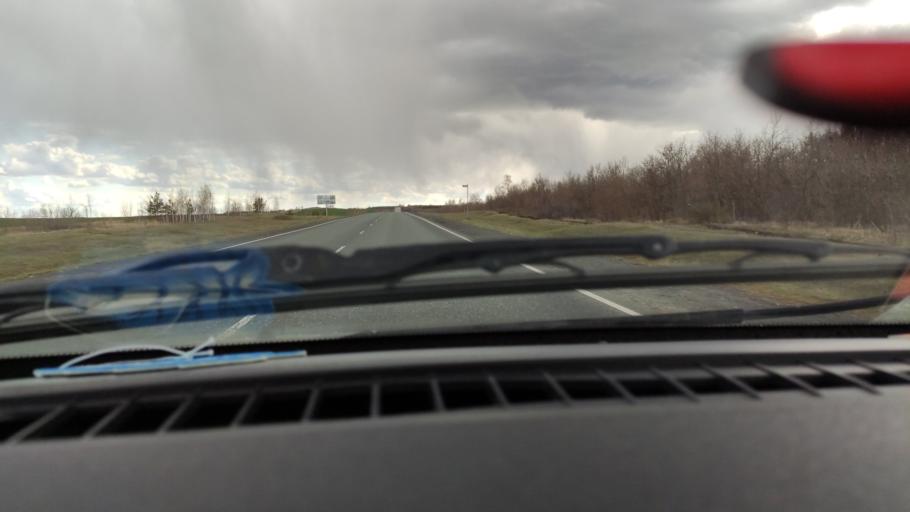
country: RU
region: Saratov
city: Balakovo
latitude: 52.1785
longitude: 47.8390
